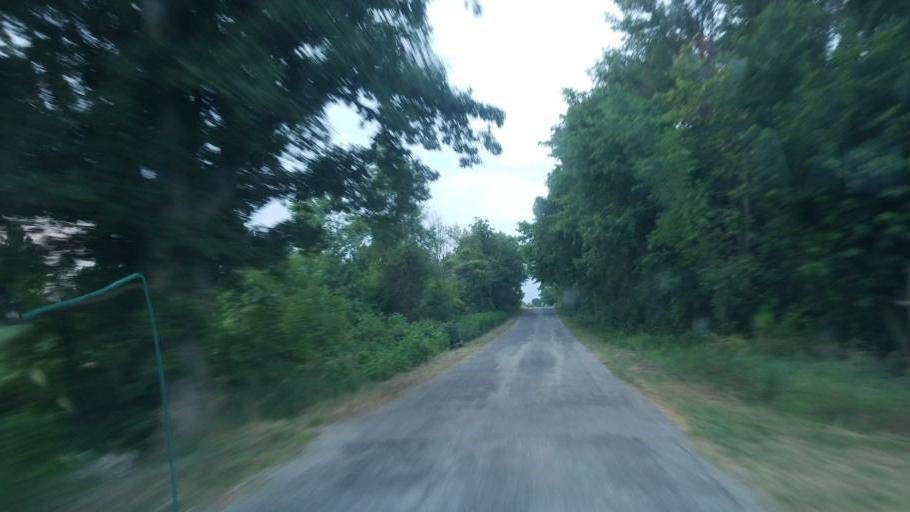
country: US
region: Ohio
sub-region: Defiance County
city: Hicksville
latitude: 41.3371
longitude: -84.8304
